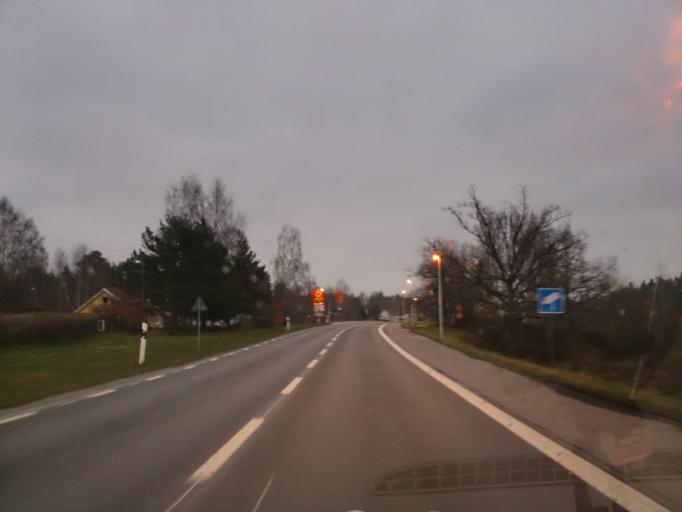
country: SE
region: OEstergoetland
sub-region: Linkopings Kommun
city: Sturefors
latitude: 58.3127
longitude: 15.8751
